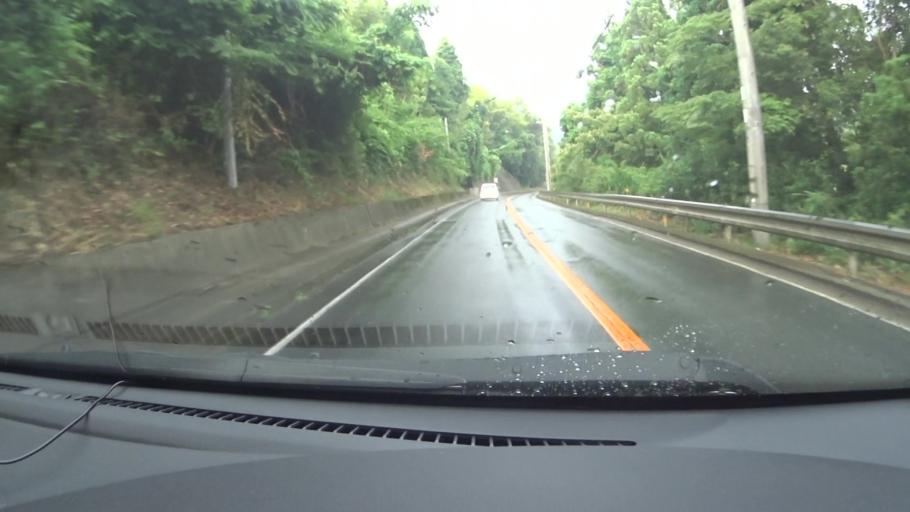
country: JP
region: Kyoto
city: Ayabe
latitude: 35.2892
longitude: 135.2952
